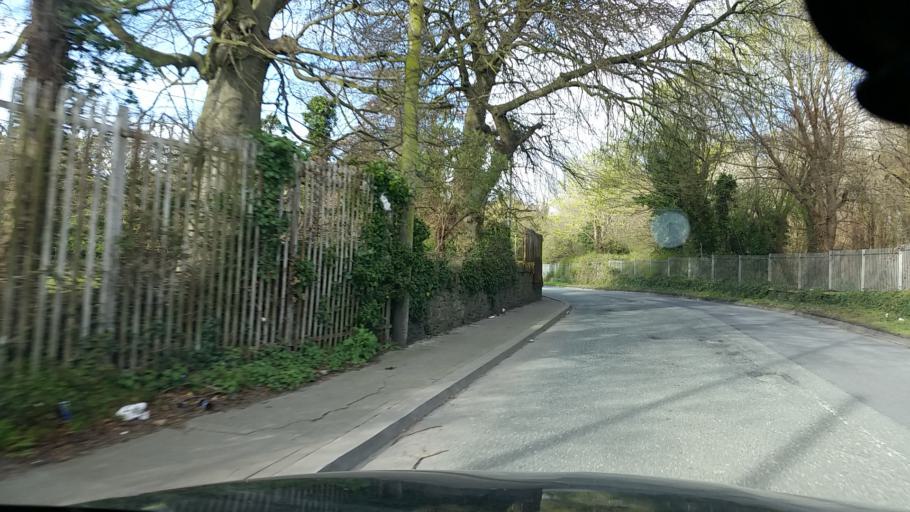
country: IE
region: Leinster
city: Ballymun
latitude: 53.4052
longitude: -6.2635
